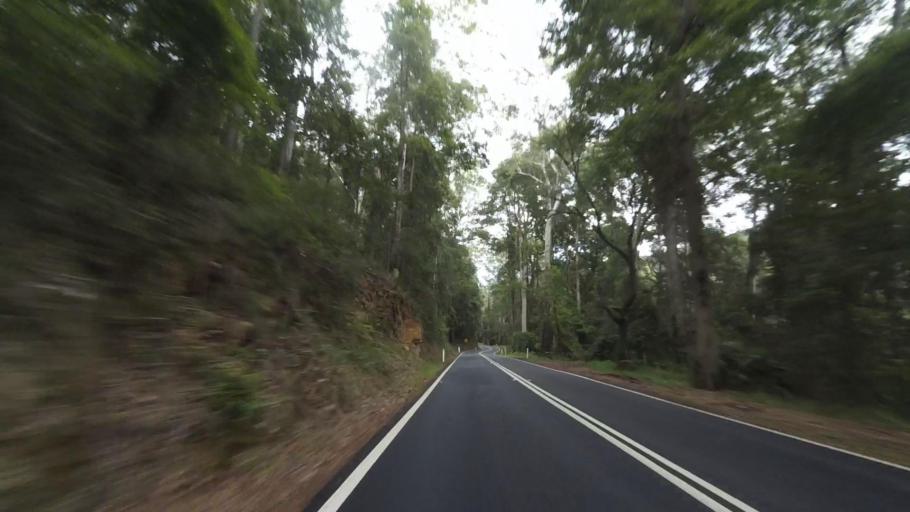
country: AU
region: New South Wales
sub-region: Wollongong
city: Helensburgh
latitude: -34.1577
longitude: 151.0183
